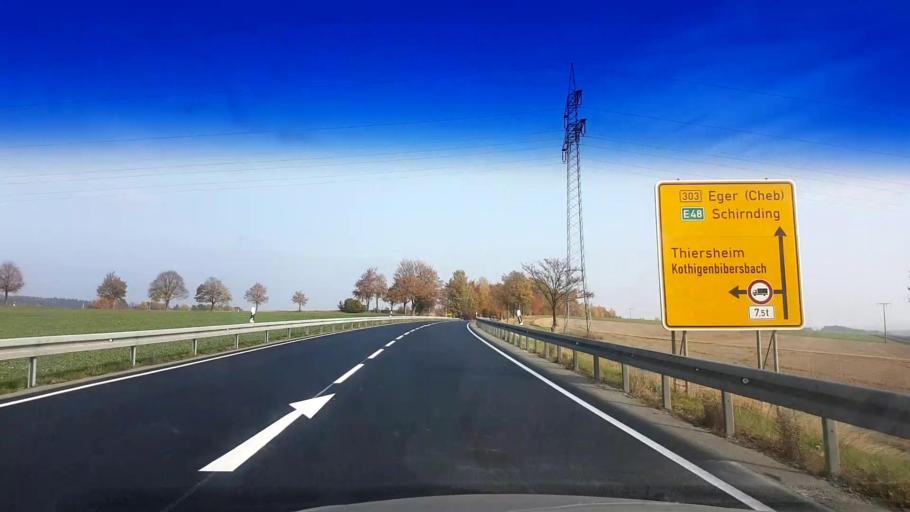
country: DE
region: Bavaria
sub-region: Upper Franconia
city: Arzberg
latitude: 50.0724
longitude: 12.1883
